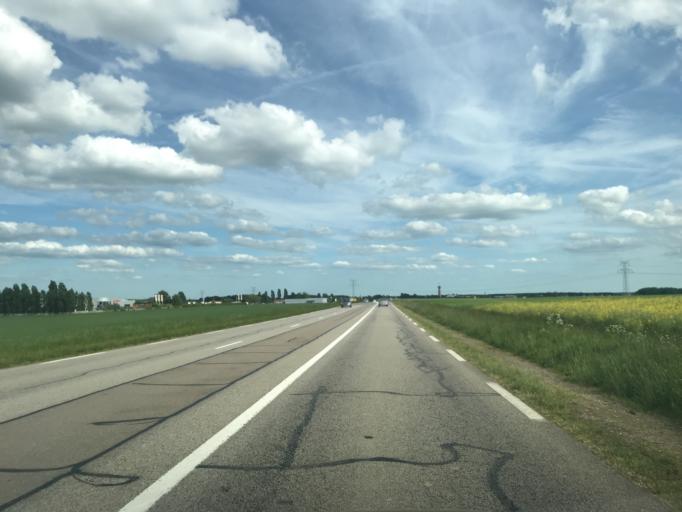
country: FR
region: Haute-Normandie
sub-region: Departement de l'Eure
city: Saint-Sebastien-de-Morsent
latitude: 49.0451
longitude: 1.0727
